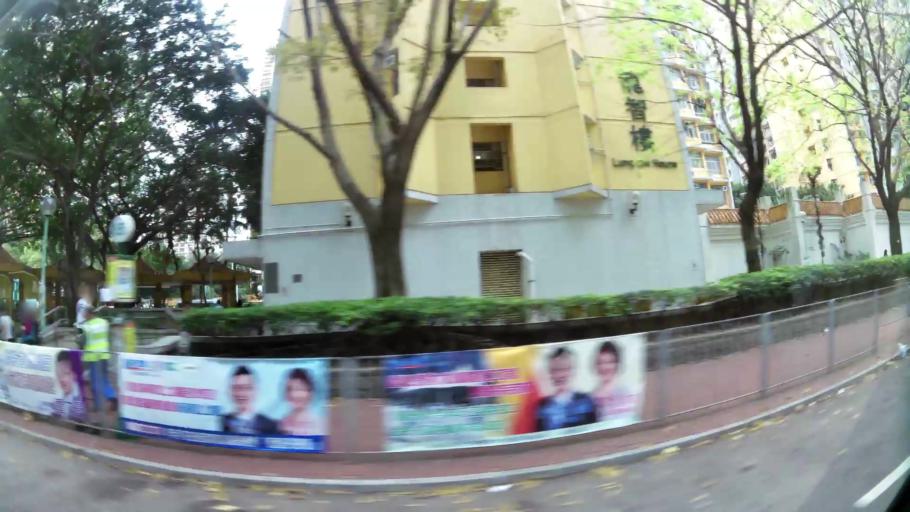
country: HK
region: Wong Tai Sin
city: Wong Tai Sin
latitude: 22.3394
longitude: 114.1938
